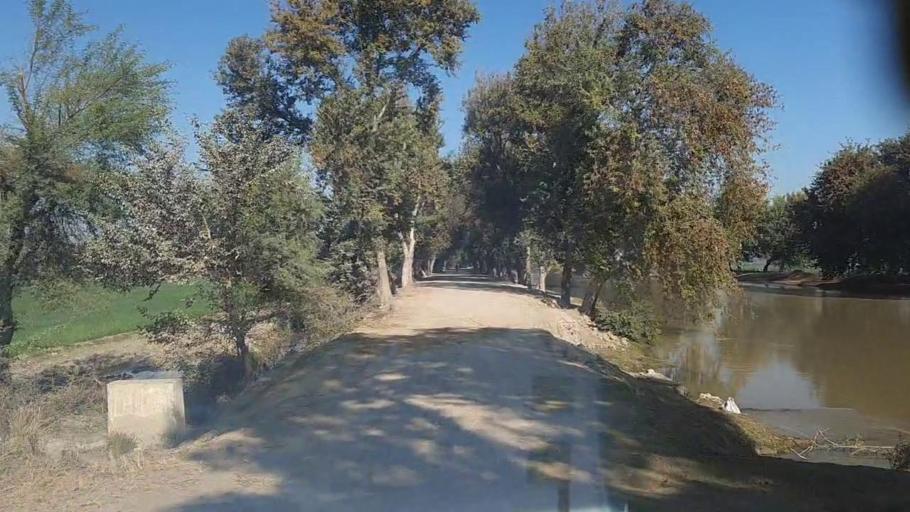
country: PK
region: Sindh
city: Khairpur
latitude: 27.9982
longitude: 69.6524
